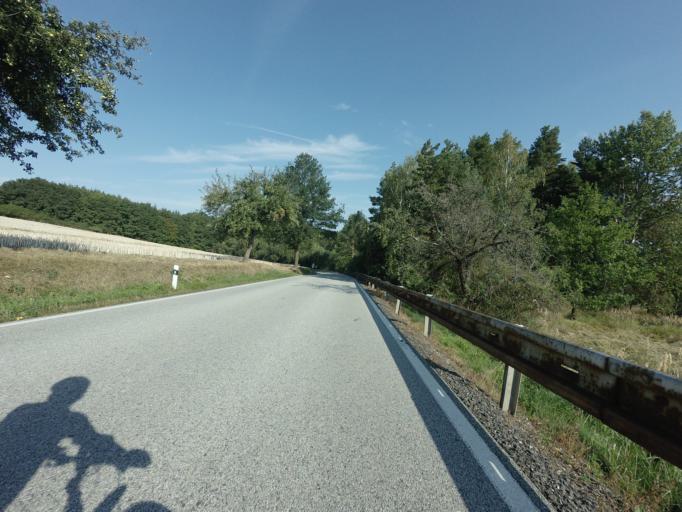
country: CZ
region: Jihocesky
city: Tyn nad Vltavou
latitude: 49.2618
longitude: 14.4128
